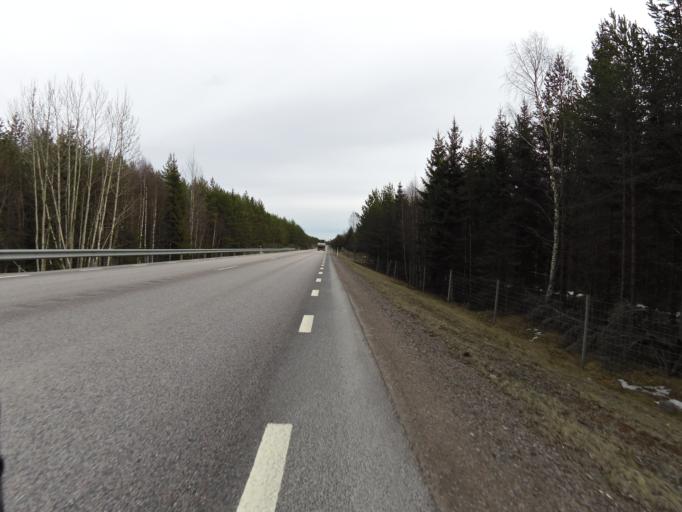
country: SE
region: Gaevleborg
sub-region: Hofors Kommun
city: Hofors
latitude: 60.5427
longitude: 16.1629
